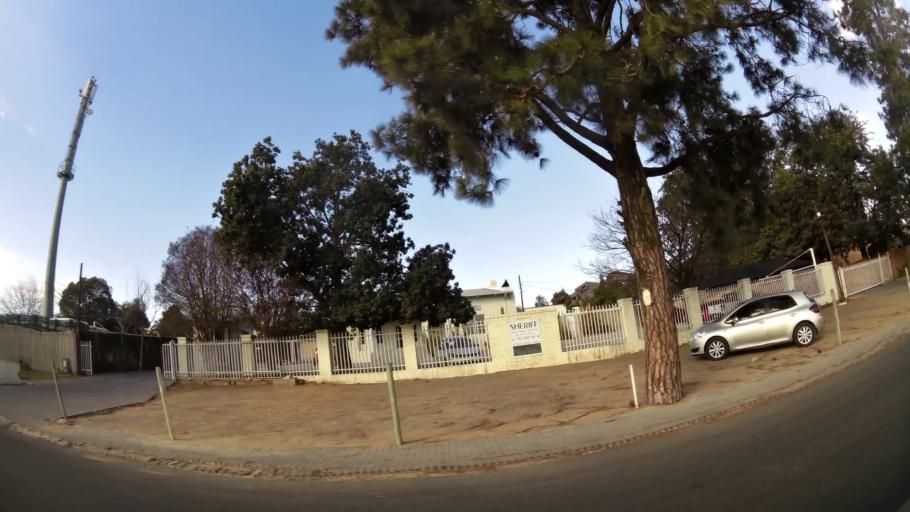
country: ZA
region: Gauteng
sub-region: City of Johannesburg Metropolitan Municipality
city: Midrand
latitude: -26.0063
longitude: 28.1256
